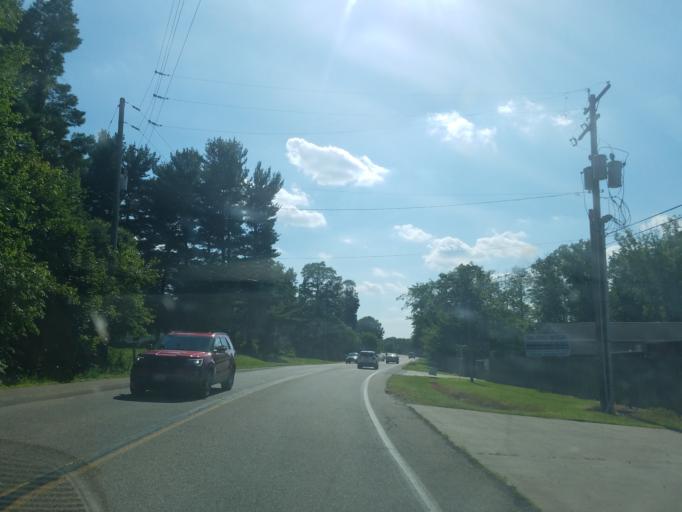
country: US
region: Ohio
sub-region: Portage County
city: Ravenna
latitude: 41.1721
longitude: -81.2672
